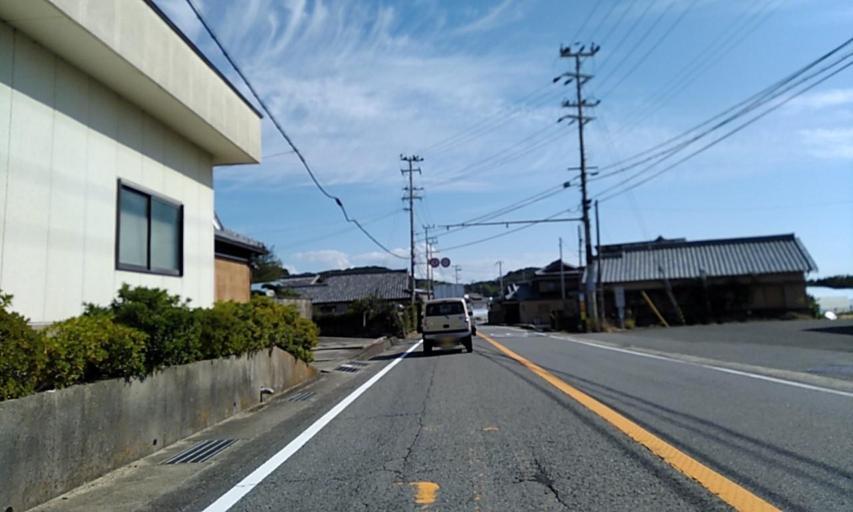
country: JP
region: Wakayama
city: Gobo
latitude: 33.8572
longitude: 135.1624
